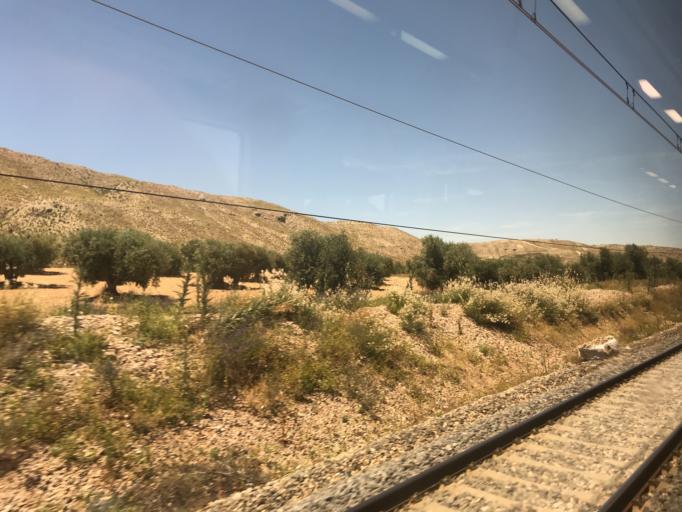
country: ES
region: Madrid
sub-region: Provincia de Madrid
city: Ciempozuelos
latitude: 40.1322
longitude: -3.6144
